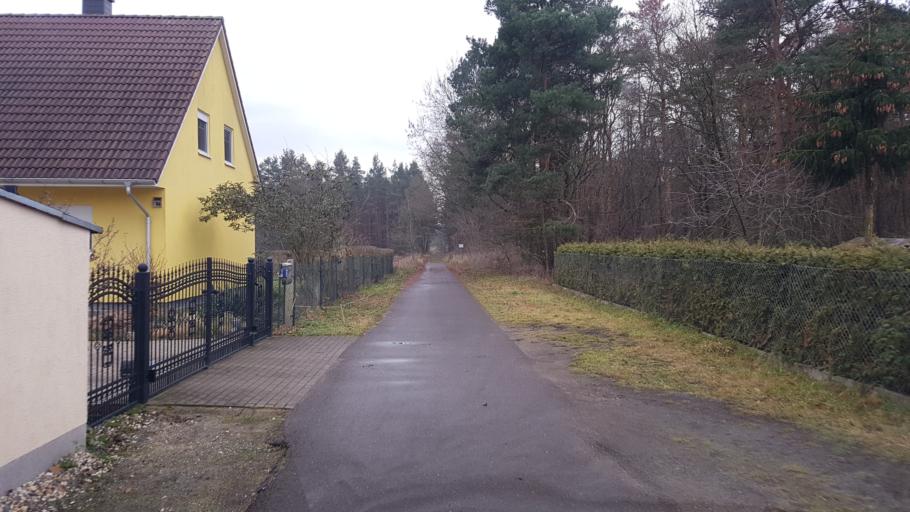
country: DE
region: Brandenburg
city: Sallgast
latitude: 51.5599
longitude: 13.8769
